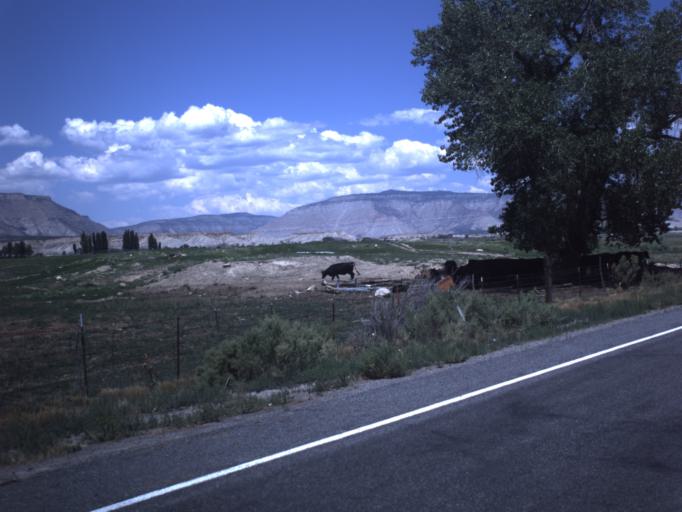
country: US
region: Utah
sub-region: Emery County
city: Castle Dale
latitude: 39.1891
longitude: -111.0477
